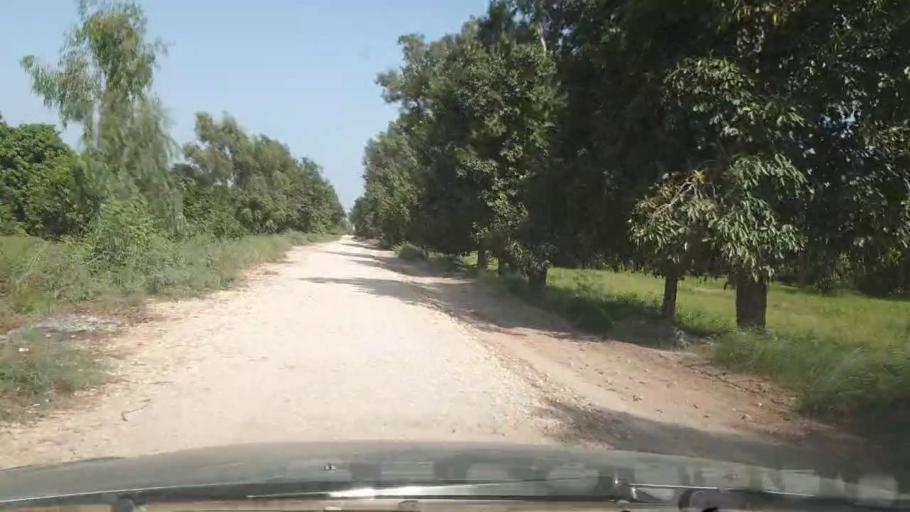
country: PK
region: Sindh
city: Tando Ghulam Ali
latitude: 25.1933
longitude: 68.8813
